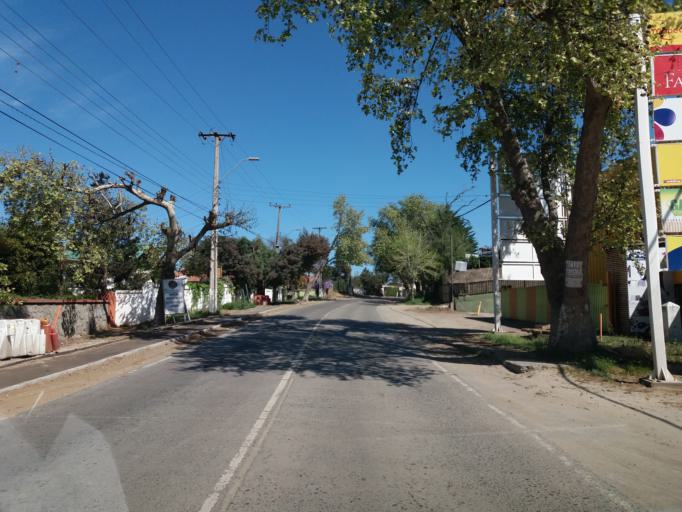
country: CL
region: Valparaiso
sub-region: Provincia de Marga Marga
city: Limache
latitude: -33.0005
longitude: -71.2095
